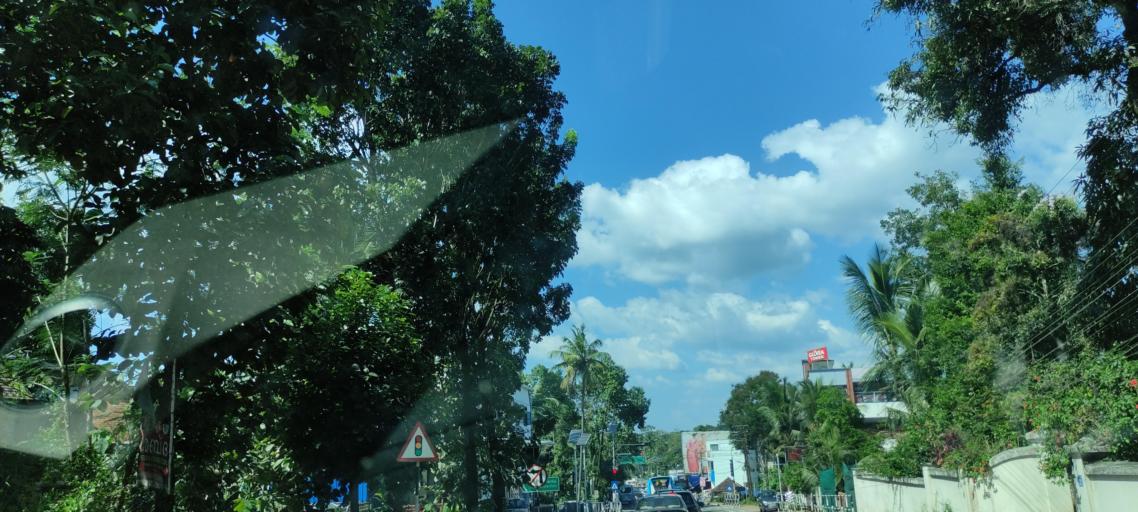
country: IN
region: Kerala
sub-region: Pattanamtitta
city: Adur
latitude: 9.1439
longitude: 76.7331
